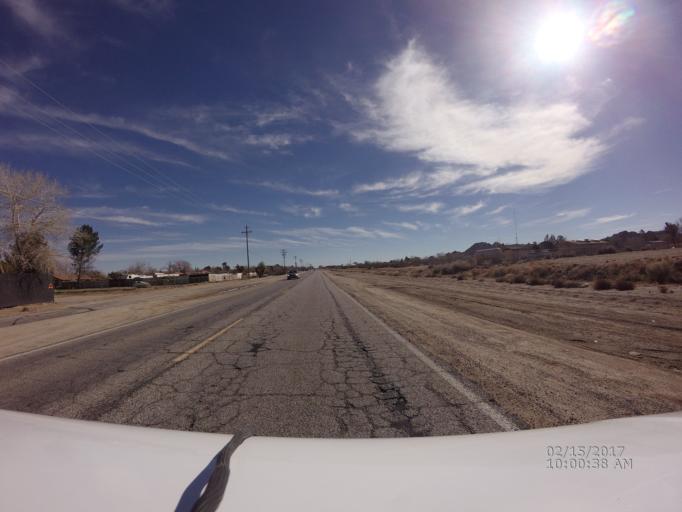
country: US
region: California
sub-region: Los Angeles County
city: Lake Los Angeles
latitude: 34.6165
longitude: -117.8348
